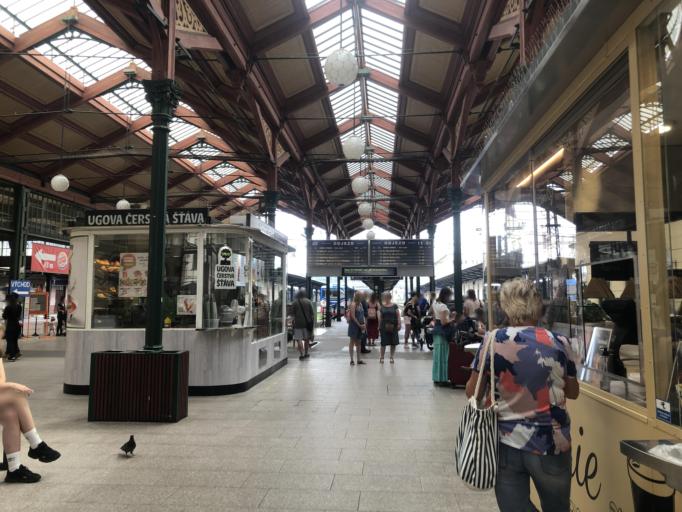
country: CZ
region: Praha
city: Prague
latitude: 50.0877
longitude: 14.4331
